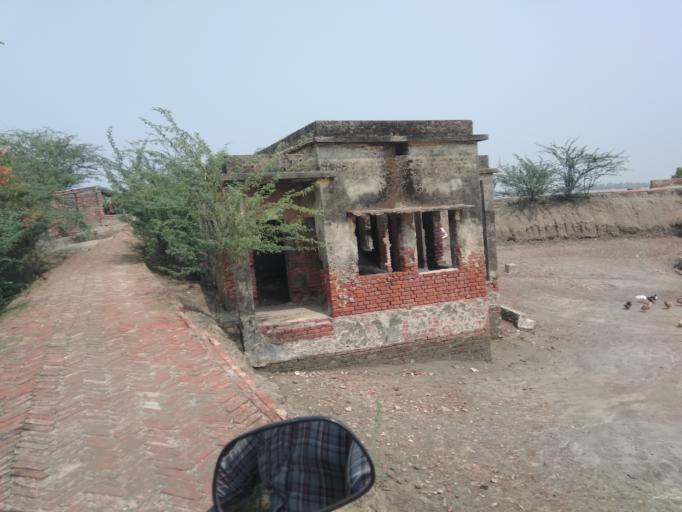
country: IN
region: West Bengal
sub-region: North 24 Parganas
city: Taki
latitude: 22.2812
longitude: 89.2841
